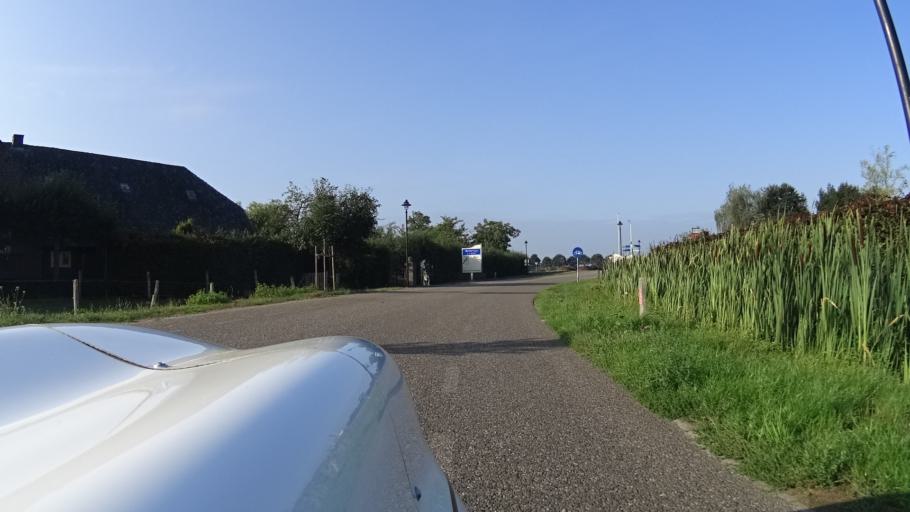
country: NL
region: Limburg
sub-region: Gemeente Bergen
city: Wellerlooi
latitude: 51.5315
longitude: 6.1337
